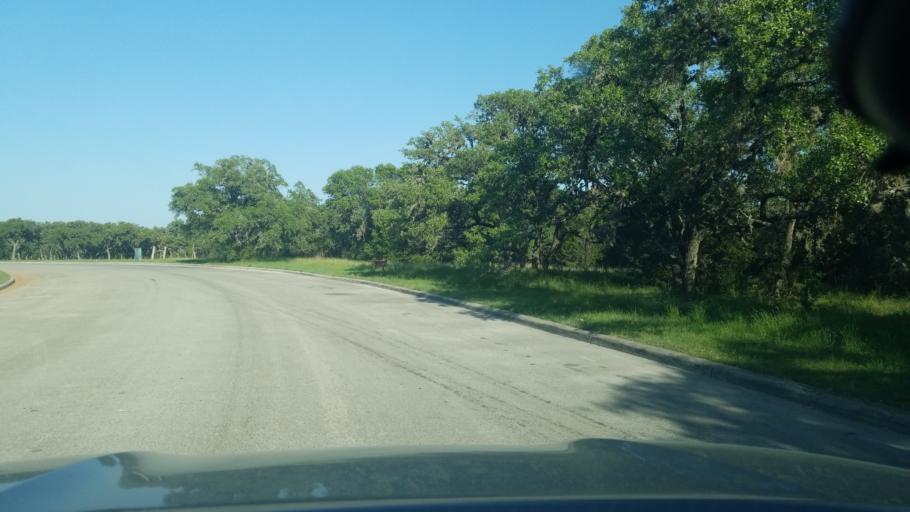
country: US
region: Texas
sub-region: Bexar County
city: Hollywood Park
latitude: 29.6080
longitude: -98.4845
